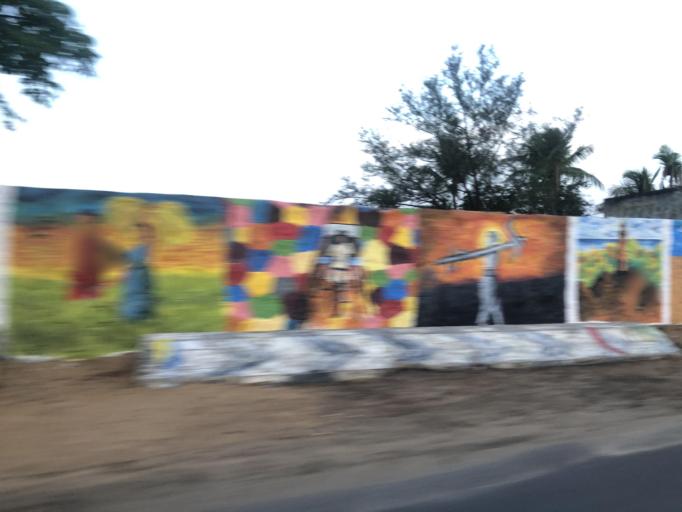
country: IN
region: Tamil Nadu
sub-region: Kancheepuram
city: Mamallapuram
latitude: 12.7476
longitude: 80.2399
